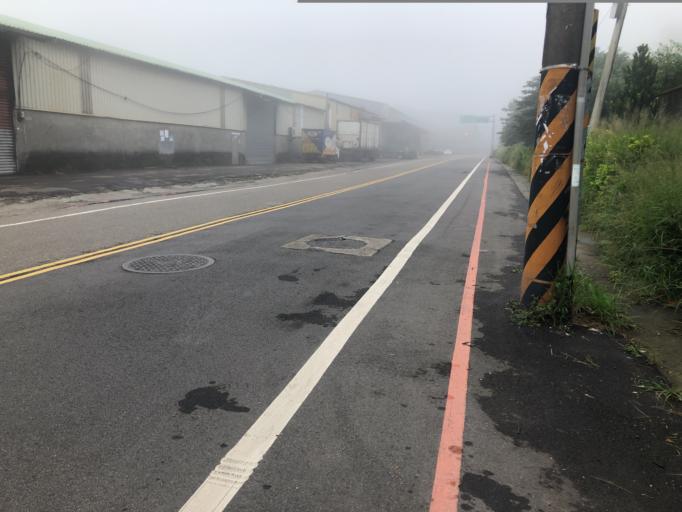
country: TW
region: Taiwan
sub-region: Taoyuan
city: Taoyuan
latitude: 25.0583
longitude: 121.3570
